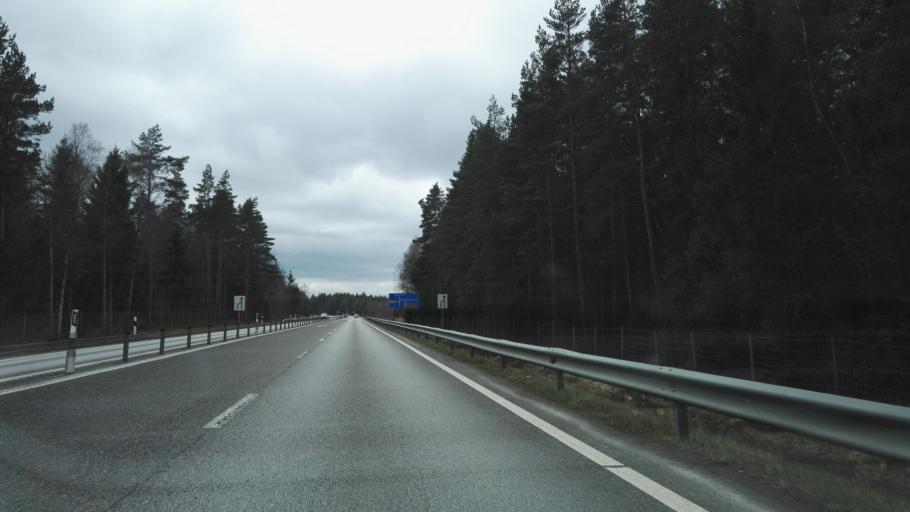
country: SE
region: Kronoberg
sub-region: Alvesta Kommun
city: Vislanda
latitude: 56.6892
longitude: 14.3261
